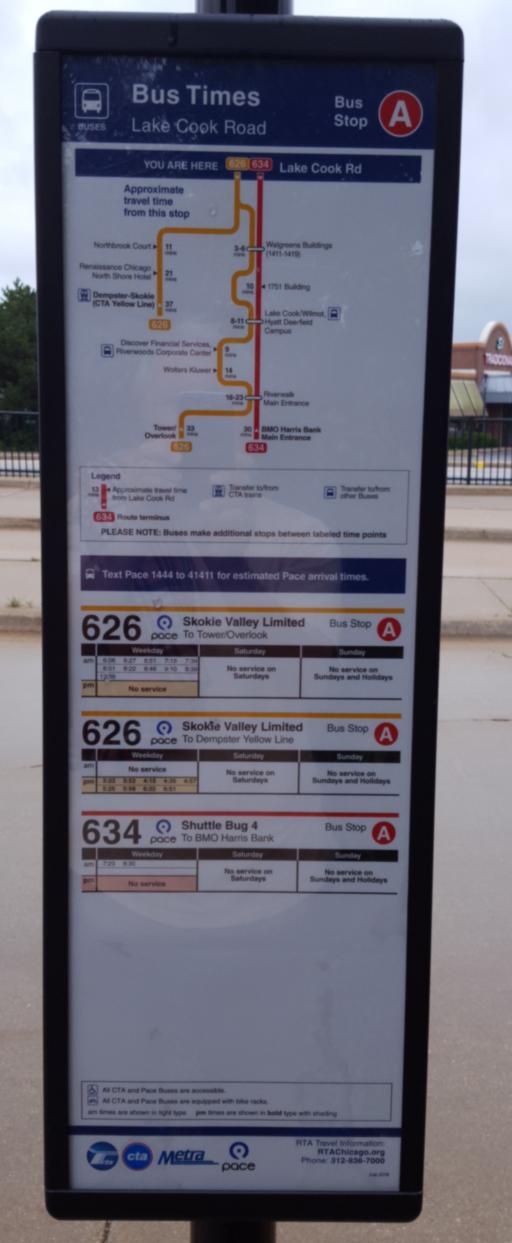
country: US
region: Illinois
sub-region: Lake County
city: Deerfield
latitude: 42.1525
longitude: -87.8416
